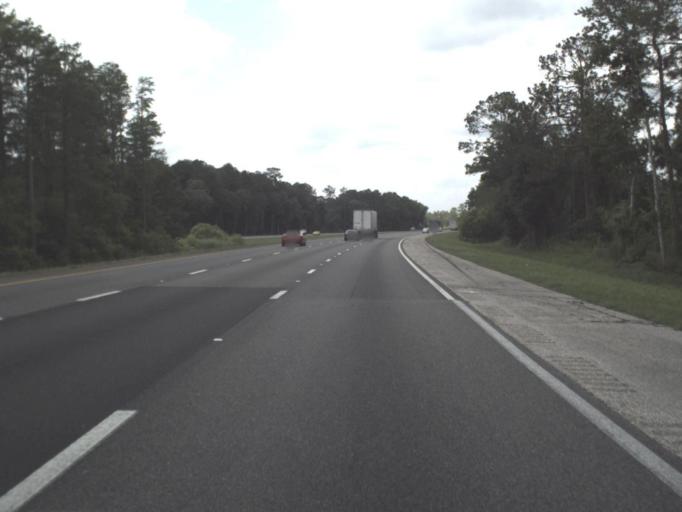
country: US
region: Florida
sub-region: Saint Johns County
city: Butler Beach
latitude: 29.6822
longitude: -81.3191
